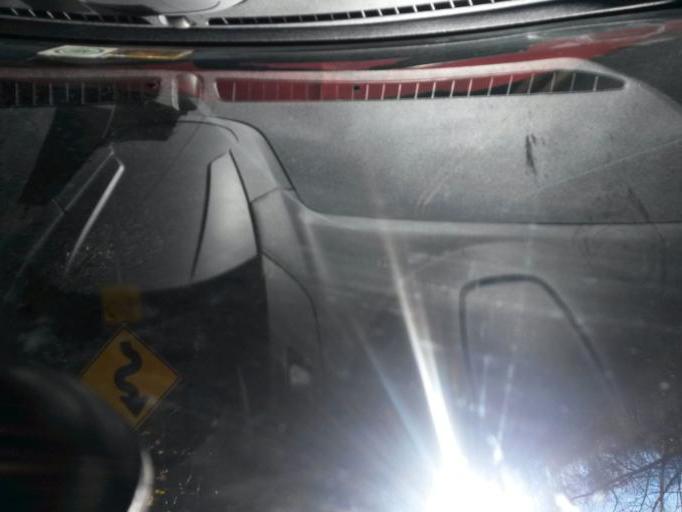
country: US
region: Virginia
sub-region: Botetourt County
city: Buchanan
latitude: 37.4996
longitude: -79.6652
